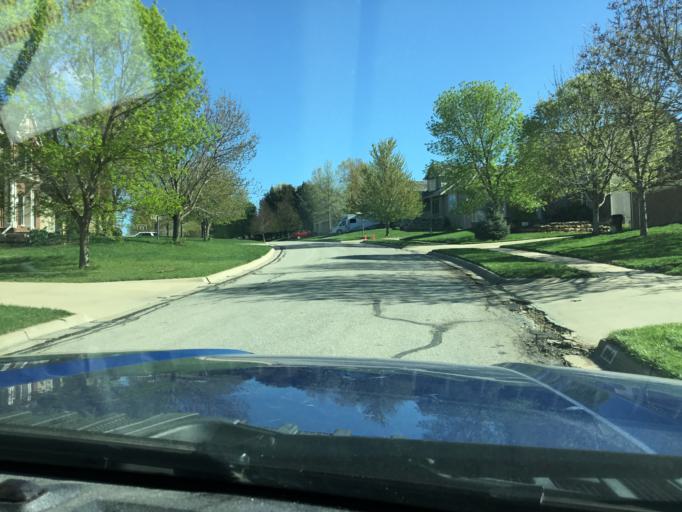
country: US
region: Kansas
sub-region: Douglas County
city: Lawrence
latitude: 38.9678
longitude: -95.3166
